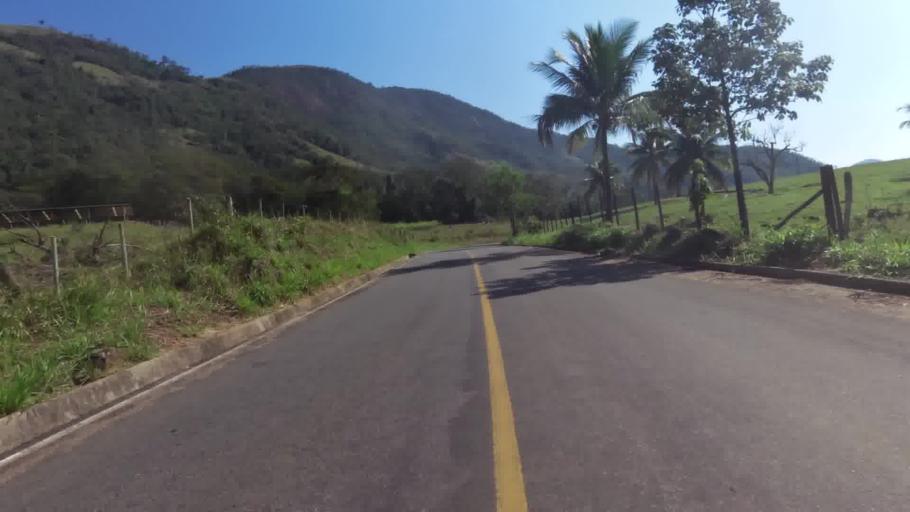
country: BR
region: Espirito Santo
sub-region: Alfredo Chaves
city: Alfredo Chaves
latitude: -20.6741
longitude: -40.7713
